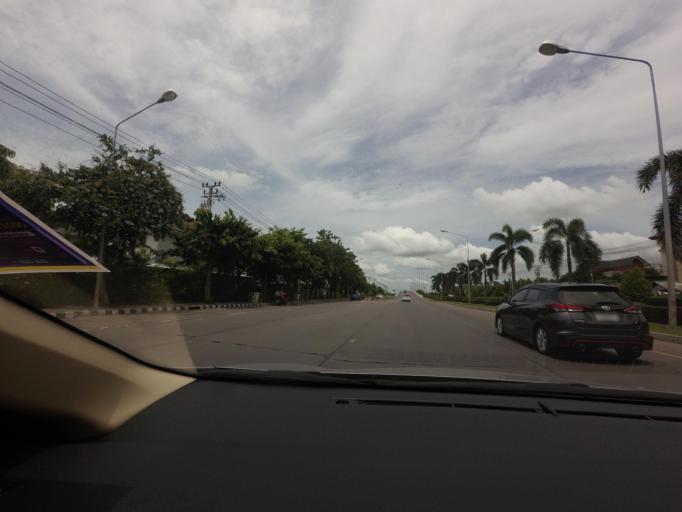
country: TH
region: Bangkok
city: Lat Krabang
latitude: 13.7194
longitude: 100.7766
